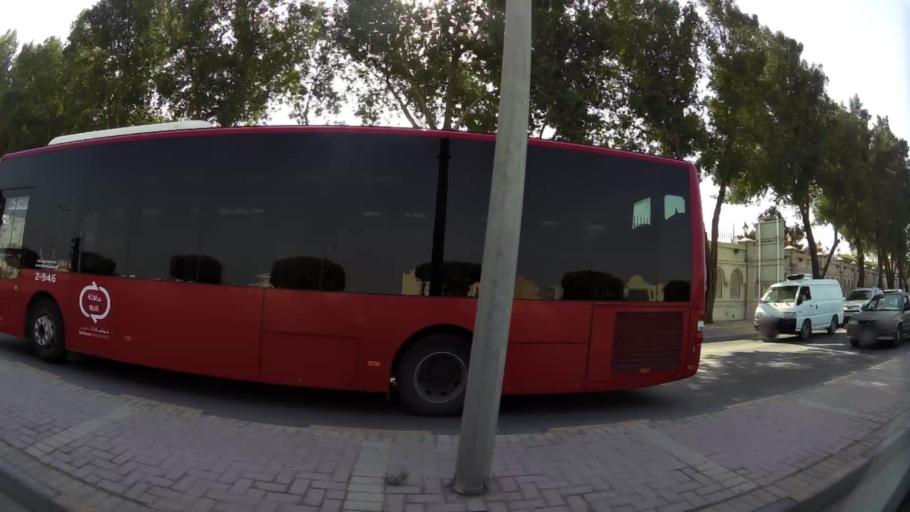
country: BH
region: Manama
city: Manama
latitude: 26.2227
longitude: 50.5866
